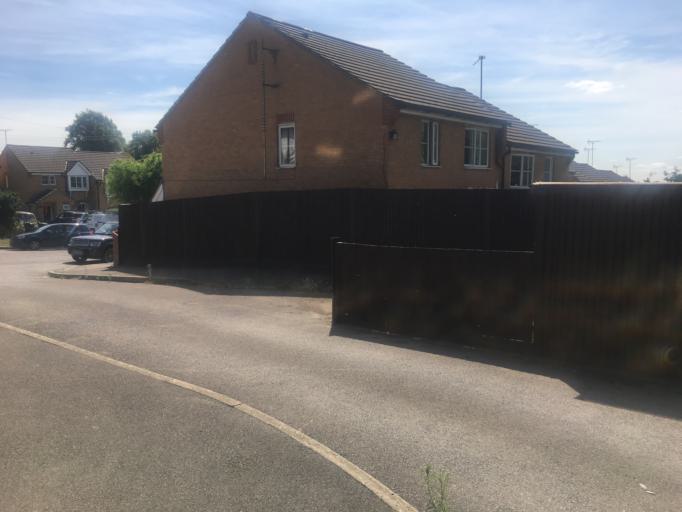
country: GB
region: England
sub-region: Surrey
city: Reigate
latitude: 51.2279
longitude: -0.1977
